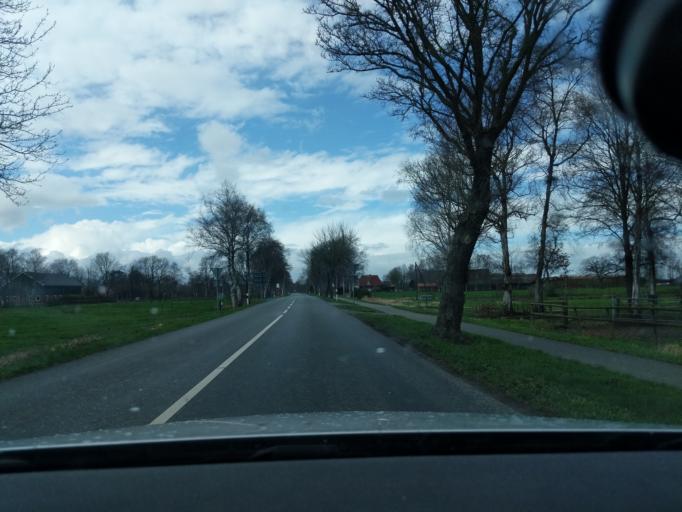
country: DE
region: Lower Saxony
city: Drochtersen
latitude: 53.6687
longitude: 9.3829
